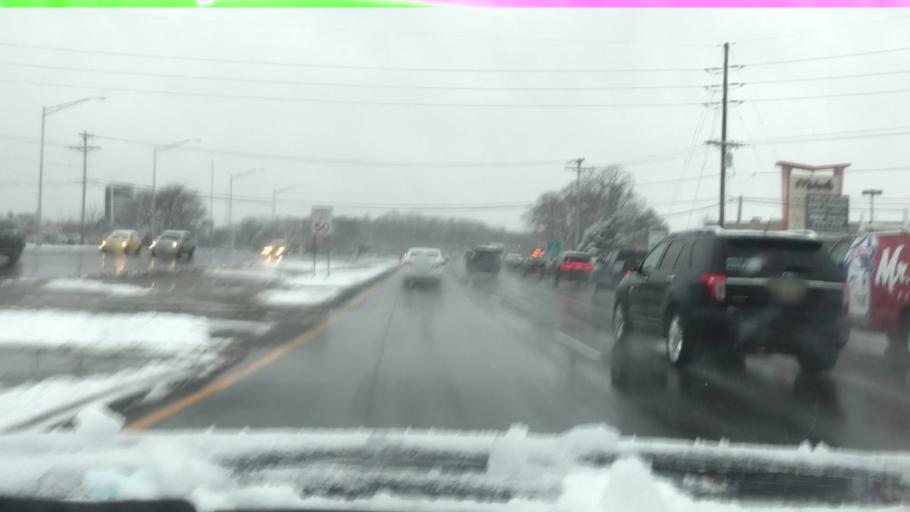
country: US
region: New Jersey
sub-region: Monmouth County
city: Eatontown
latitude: 40.2909
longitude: -74.0523
